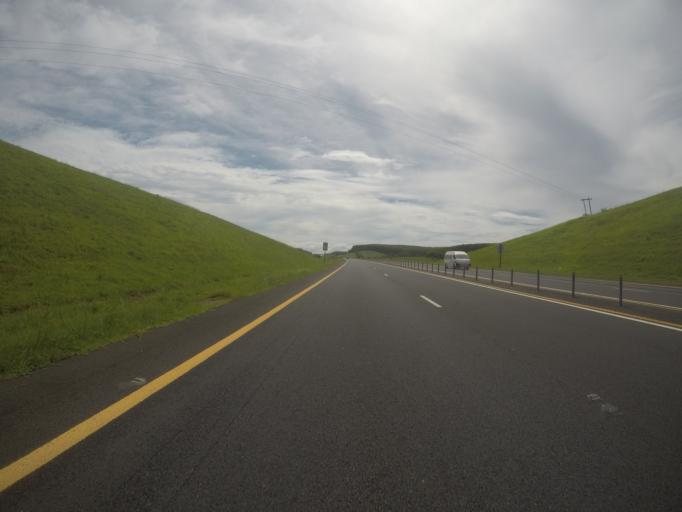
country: ZA
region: KwaZulu-Natal
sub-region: uThungulu District Municipality
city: Eshowe
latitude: -29.0479
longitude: 31.6411
